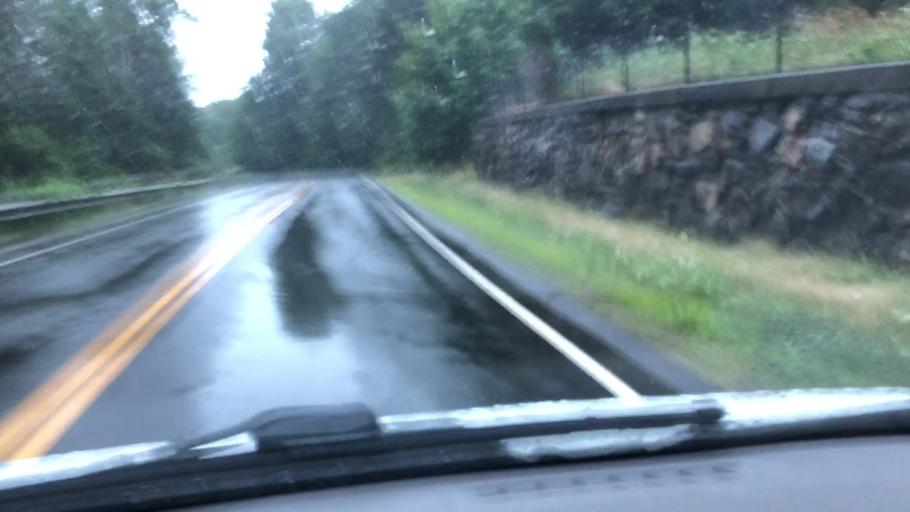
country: US
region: Massachusetts
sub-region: Hampshire County
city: Westhampton
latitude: 42.2850
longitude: -72.8341
